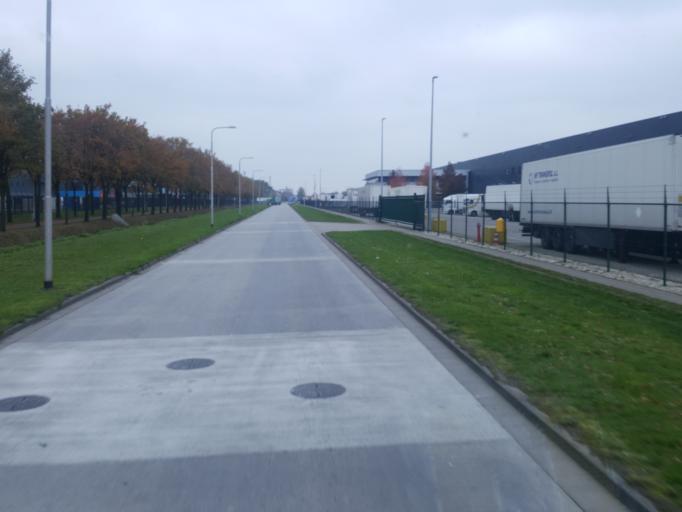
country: NL
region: North Brabant
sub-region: Gemeente Dongen
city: Dongen
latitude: 51.6022
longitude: 4.9968
